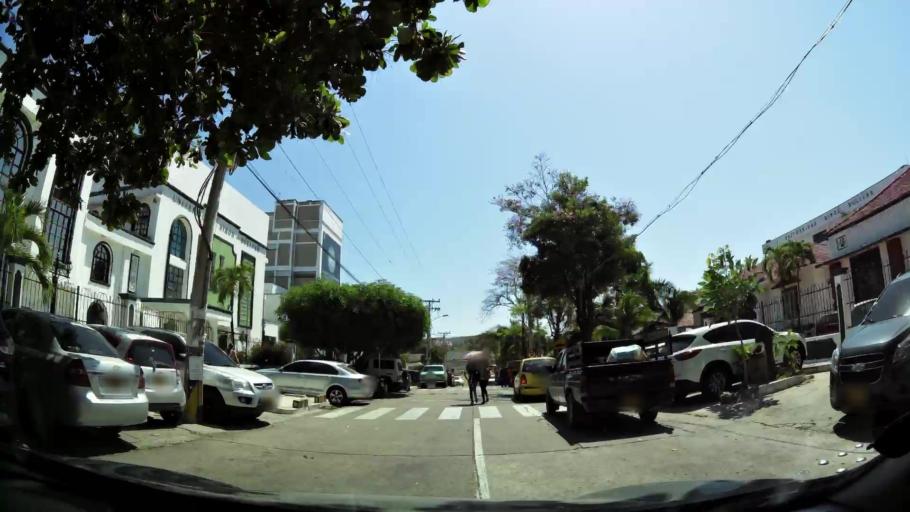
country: CO
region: Atlantico
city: Barranquilla
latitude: 10.9954
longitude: -74.7926
